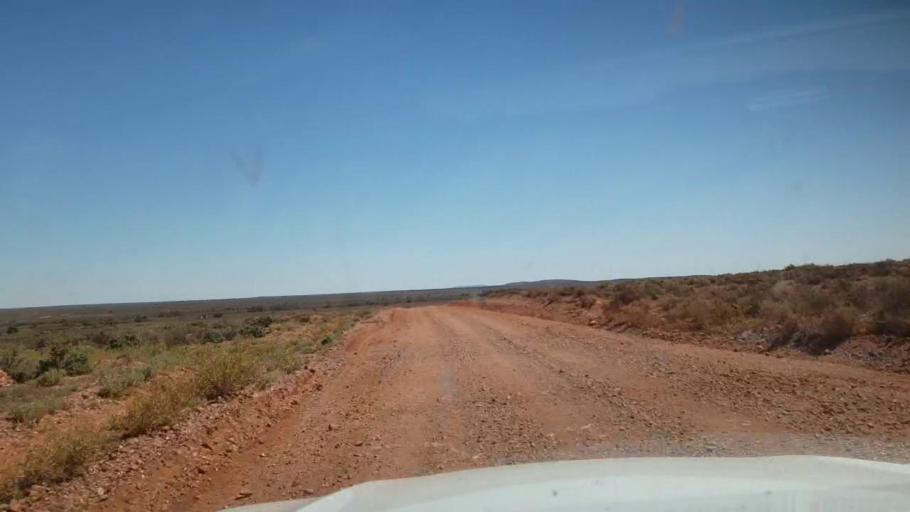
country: AU
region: South Australia
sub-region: Whyalla
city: Whyalla
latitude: -32.6856
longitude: 137.1192
